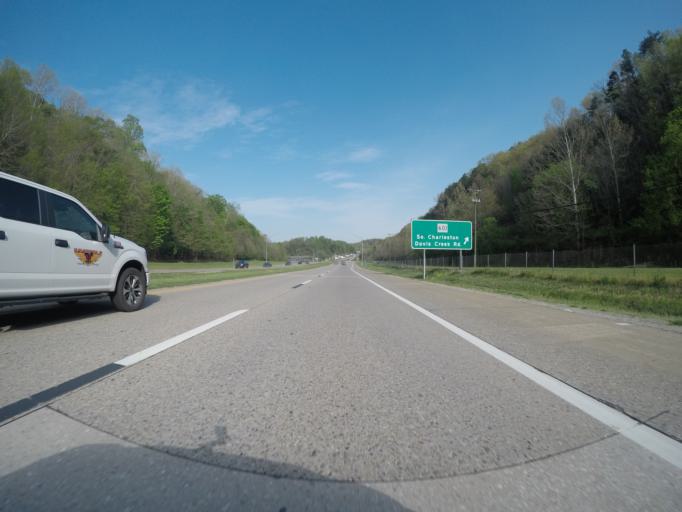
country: US
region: West Virginia
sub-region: Kanawha County
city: South Charleston
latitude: 38.3394
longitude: -81.6965
